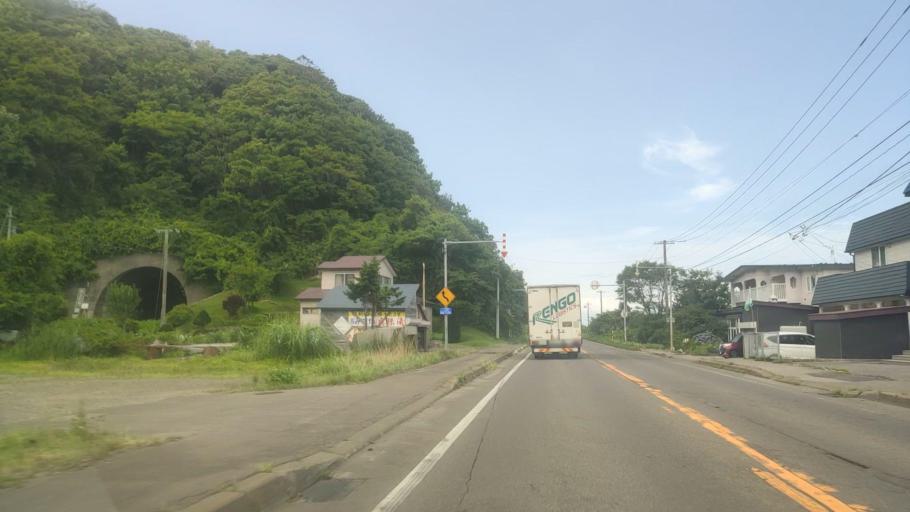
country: JP
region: Hokkaido
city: Nanae
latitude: 42.1614
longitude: 140.4705
